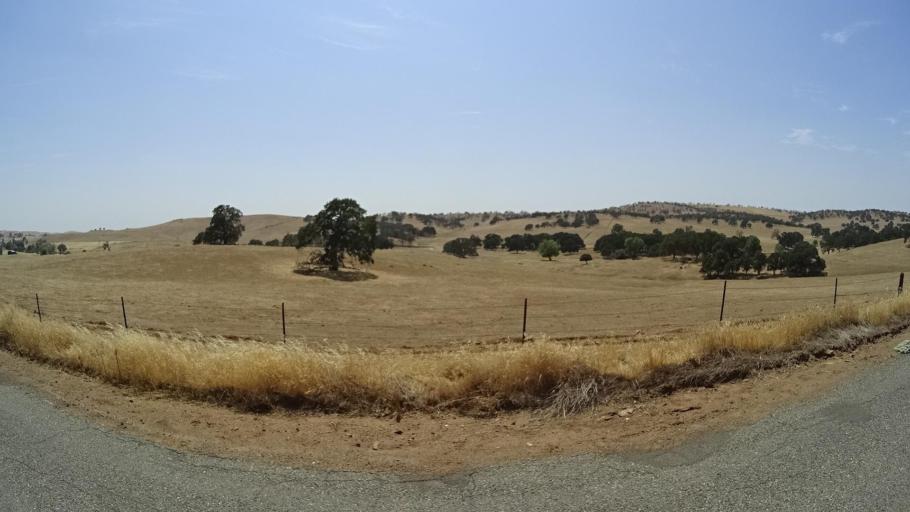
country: US
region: California
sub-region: Merced County
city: Planada
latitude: 37.5134
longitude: -120.2400
